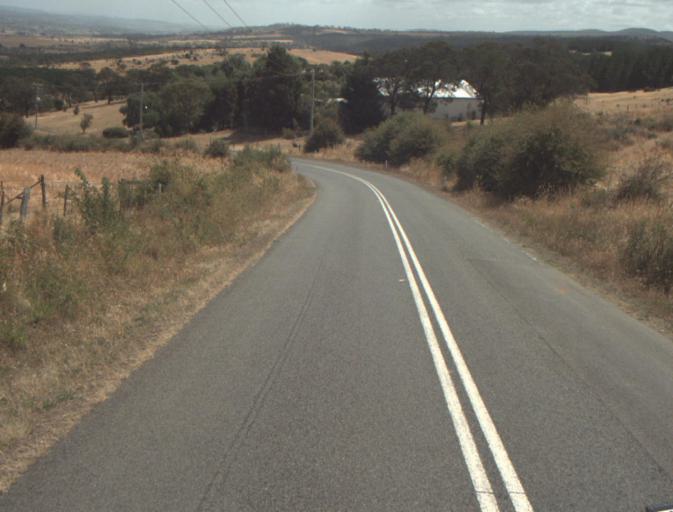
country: AU
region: Tasmania
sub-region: Northern Midlands
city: Evandale
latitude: -41.5103
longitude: 147.2882
